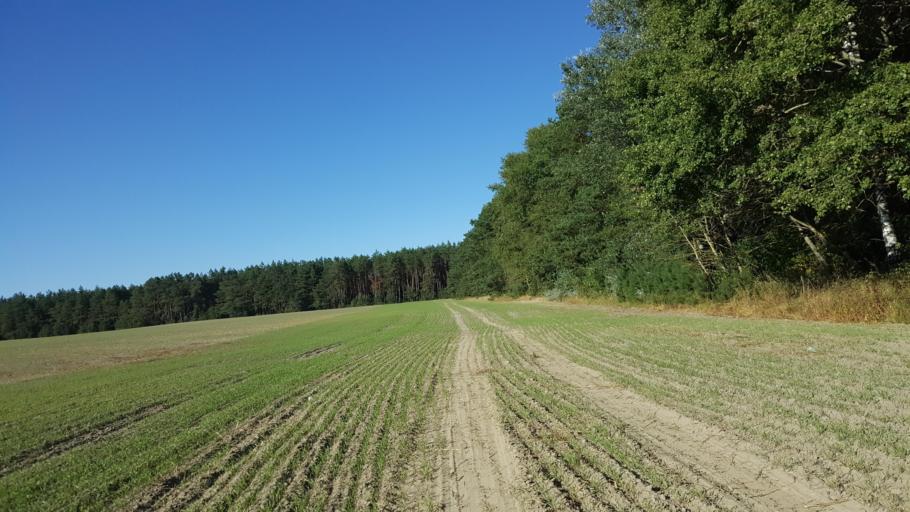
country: PL
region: Lublin Voivodeship
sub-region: Powiat bialski
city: Janow Podlaski
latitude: 52.3016
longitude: 23.2472
